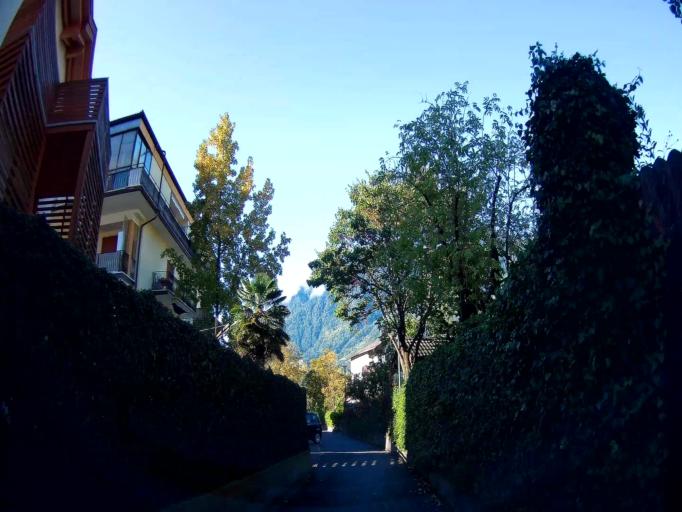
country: IT
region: Trentino-Alto Adige
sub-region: Bolzano
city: Merano
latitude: 46.6608
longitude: 11.1688
